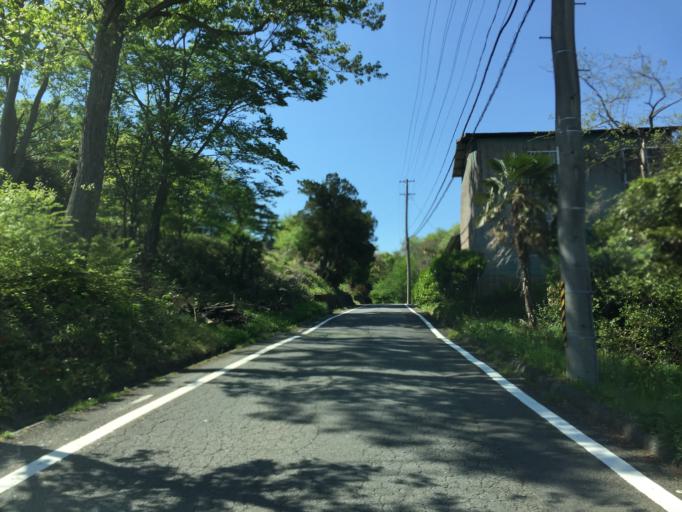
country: JP
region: Fukushima
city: Iwaki
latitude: 37.0544
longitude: 140.7964
